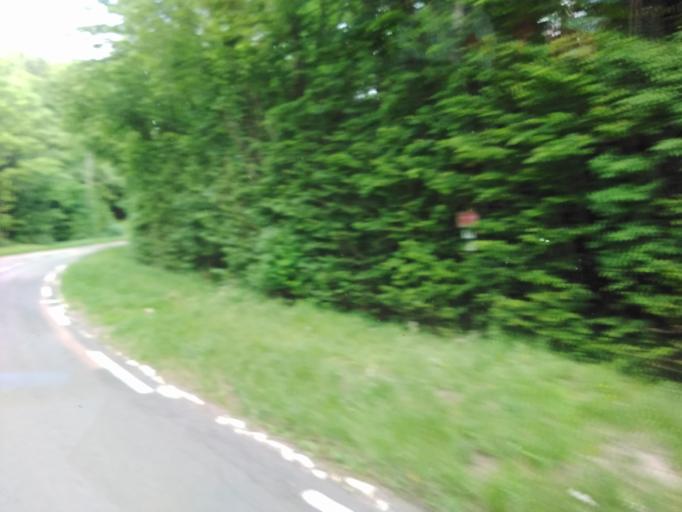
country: FR
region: Franche-Comte
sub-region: Departement du Jura
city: Arbois
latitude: 46.8658
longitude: 5.8055
